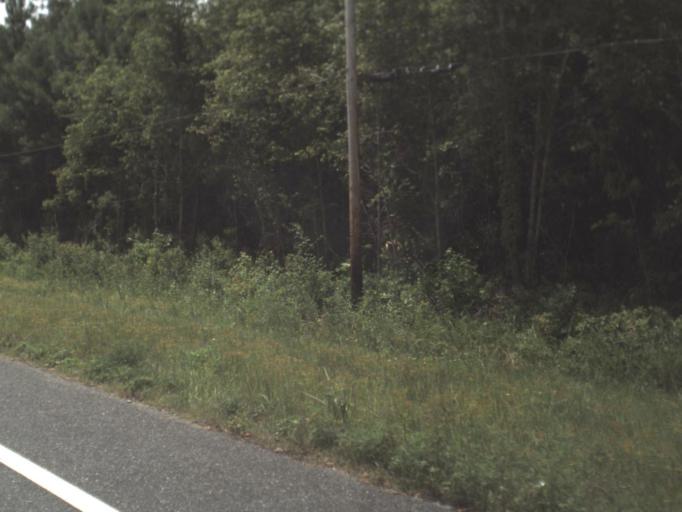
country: US
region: Florida
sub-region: Columbia County
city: Watertown
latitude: 30.1607
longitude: -82.5670
